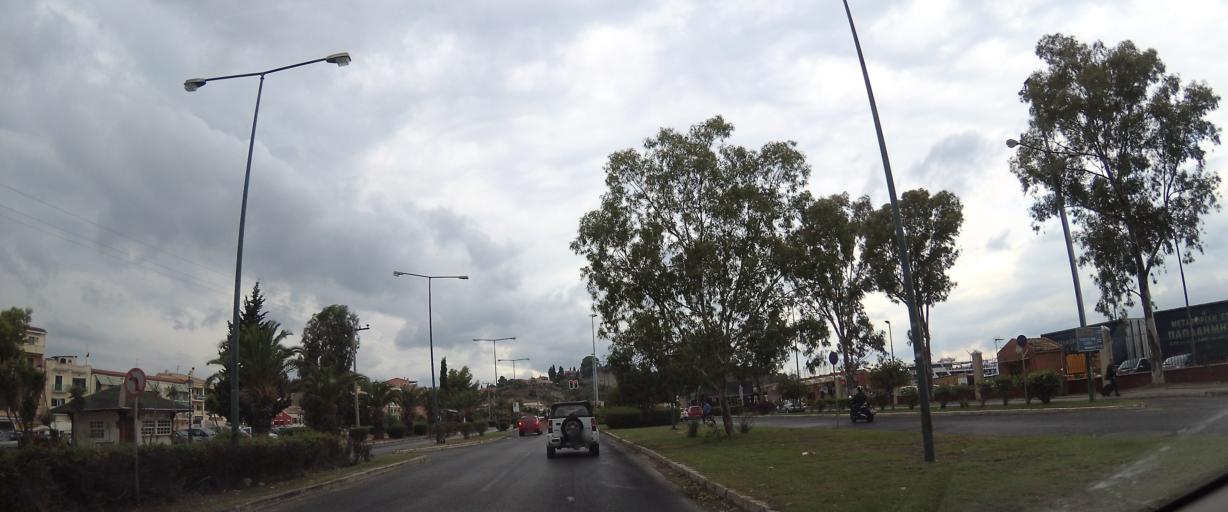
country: GR
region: Ionian Islands
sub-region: Nomos Kerkyras
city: Alepou
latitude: 39.6267
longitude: 19.9052
